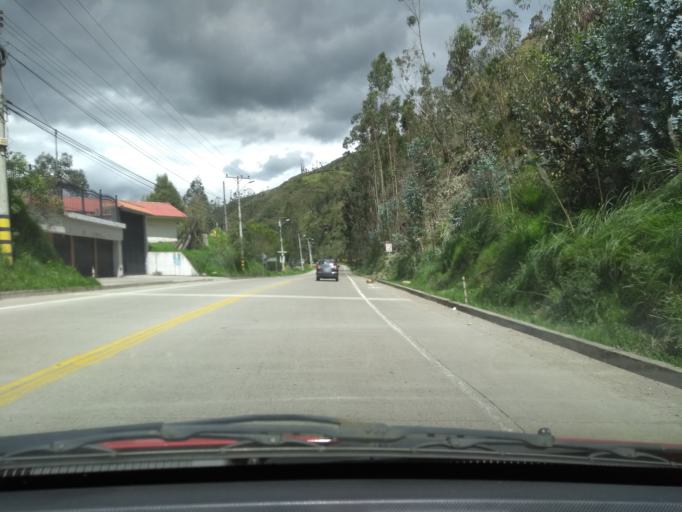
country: EC
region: Azuay
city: Cuenca
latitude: -2.9641
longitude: -79.0496
